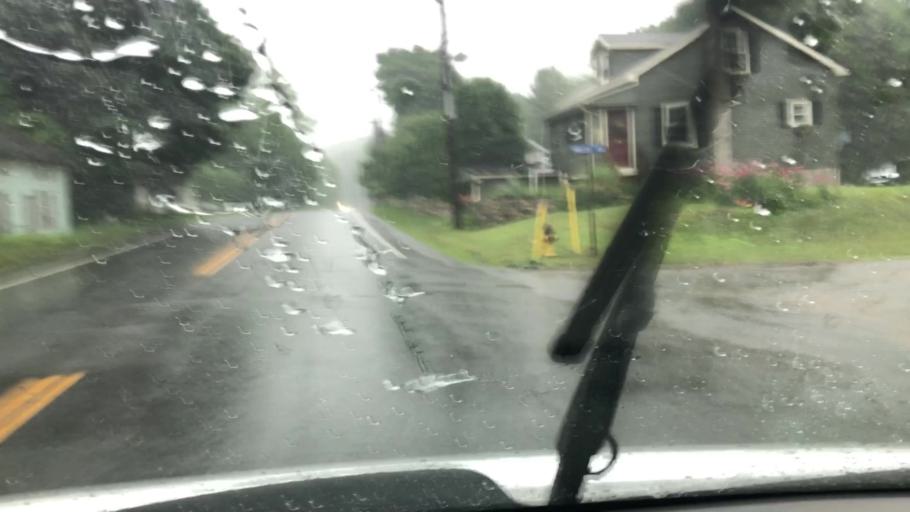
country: US
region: Massachusetts
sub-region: Berkshire County
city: Adams
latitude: 42.6059
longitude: -73.1339
